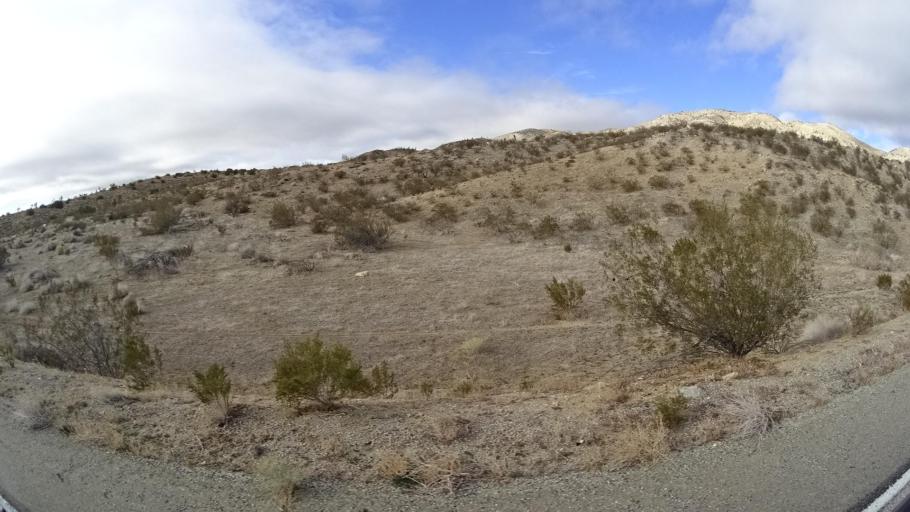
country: US
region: California
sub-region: Kern County
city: Tehachapi
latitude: 35.0044
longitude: -118.3392
